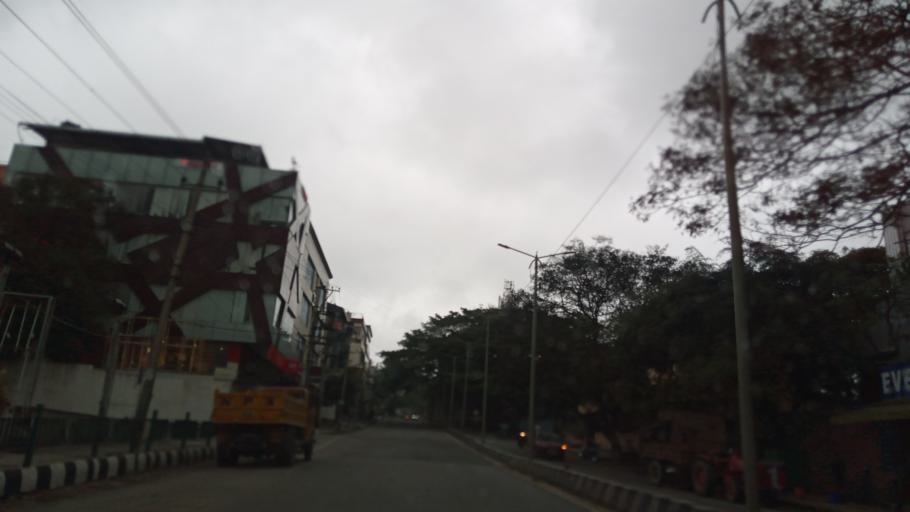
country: IN
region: Karnataka
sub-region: Bangalore Urban
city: Bangalore
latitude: 12.9228
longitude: 77.5604
